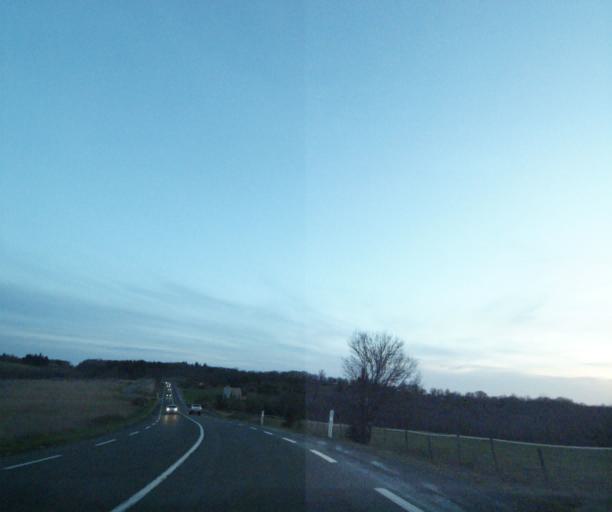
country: FR
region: Midi-Pyrenees
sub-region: Departement du Lot
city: Pradines
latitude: 44.5166
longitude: 1.4446
